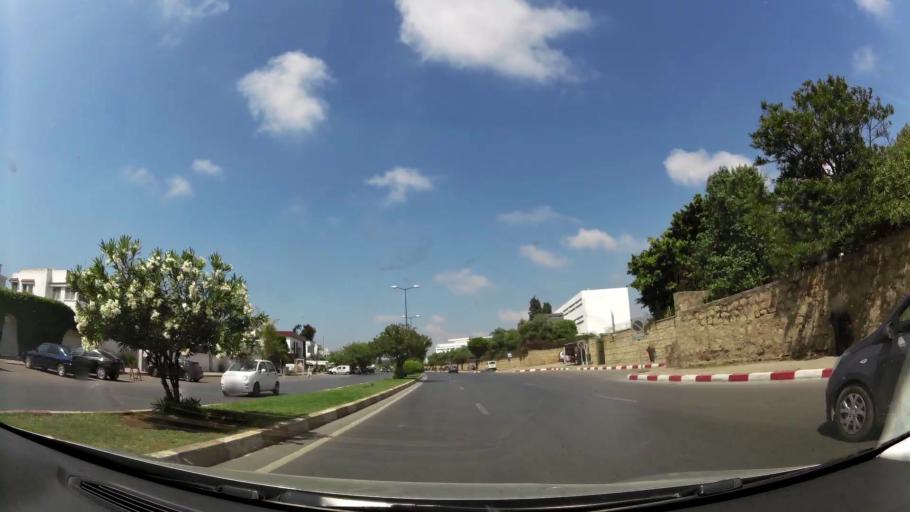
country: MA
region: Rabat-Sale-Zemmour-Zaer
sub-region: Rabat
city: Rabat
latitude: 33.9899
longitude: -6.8476
